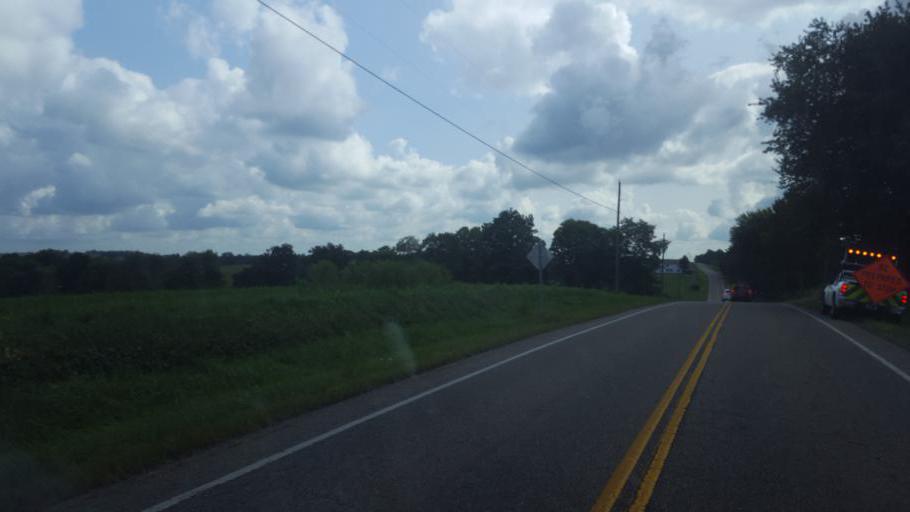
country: US
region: Ohio
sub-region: Stark County
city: Louisville
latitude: 40.7988
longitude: -81.2059
